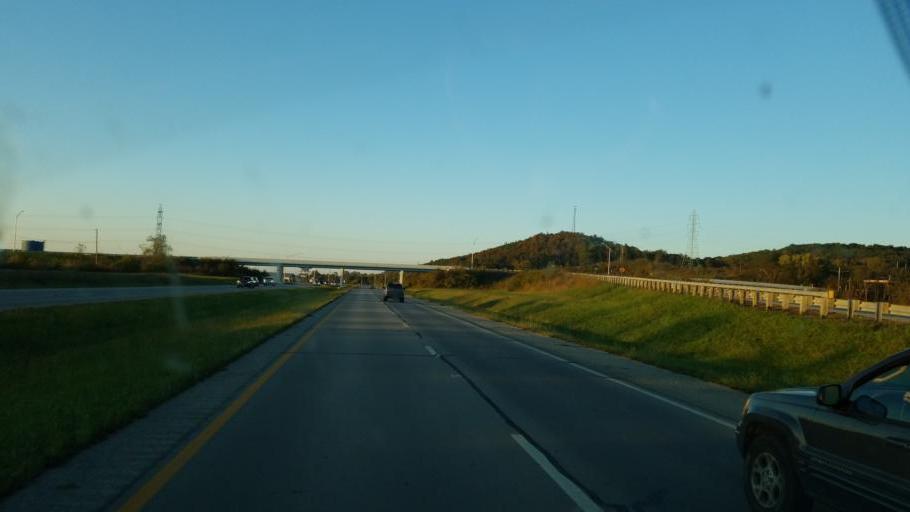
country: US
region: Ohio
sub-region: Pike County
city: Piketon
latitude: 39.0109
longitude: -83.0260
